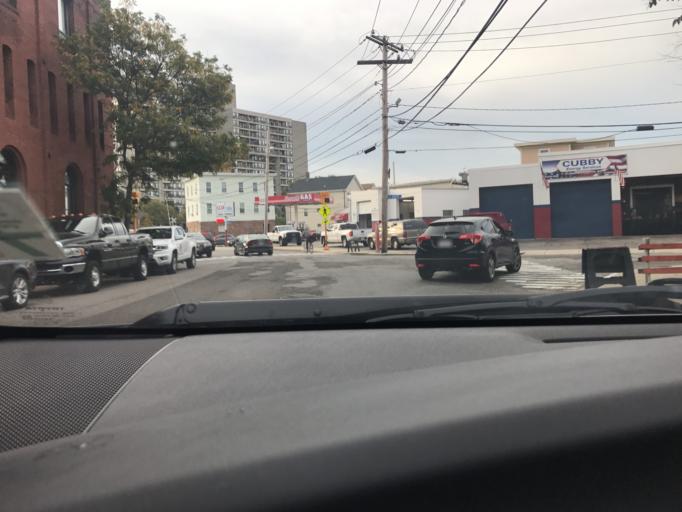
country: US
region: Massachusetts
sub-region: Middlesex County
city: Somerville
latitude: 42.3744
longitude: -71.0882
